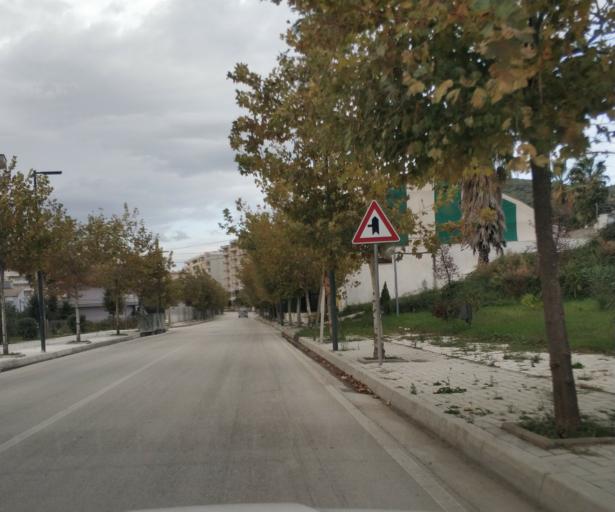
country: AL
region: Vlore
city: Vlore
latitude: 40.4388
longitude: 19.4969
